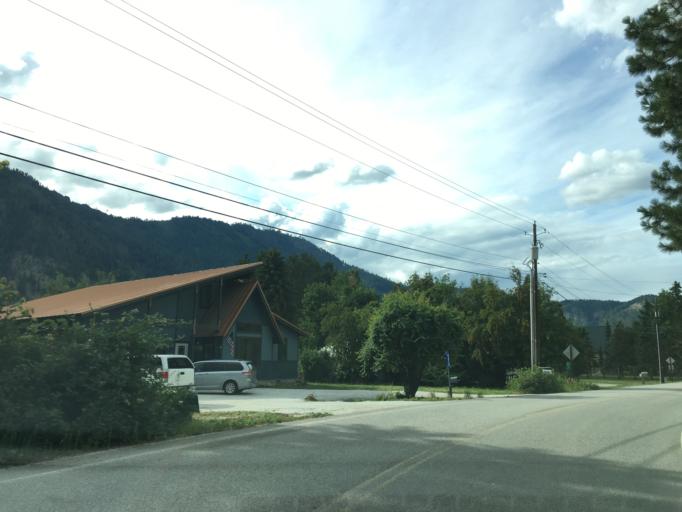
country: US
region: Washington
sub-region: Chelan County
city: Leavenworth
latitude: 47.5863
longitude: -120.6596
